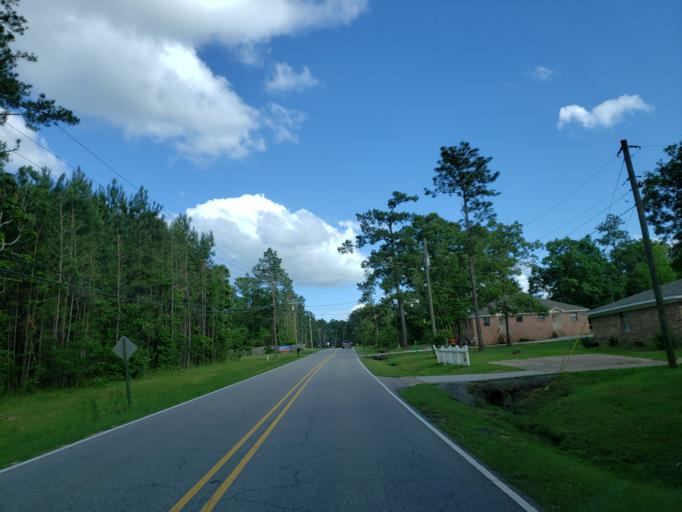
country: US
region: Mississippi
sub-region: Lamar County
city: West Hattiesburg
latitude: 31.2876
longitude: -89.4407
